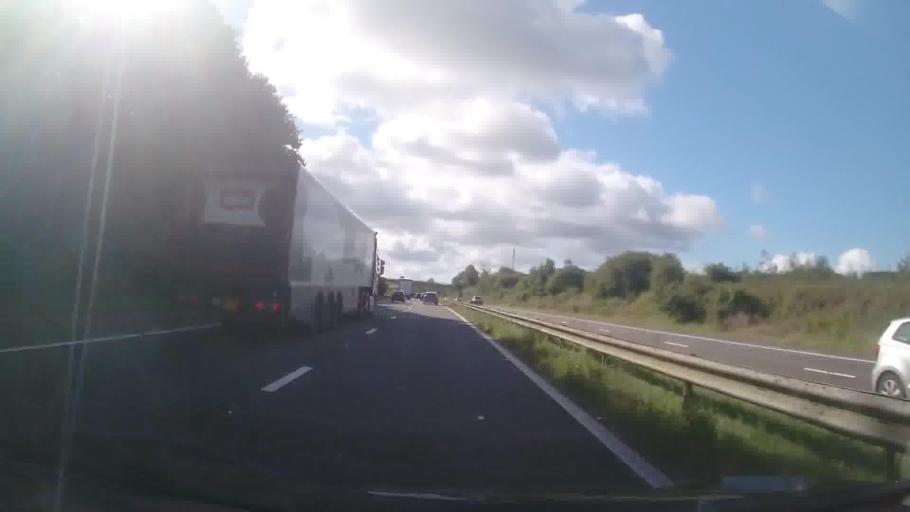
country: GB
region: Wales
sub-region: City and County of Swansea
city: Pontarddulais
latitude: 51.7370
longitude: -4.0696
